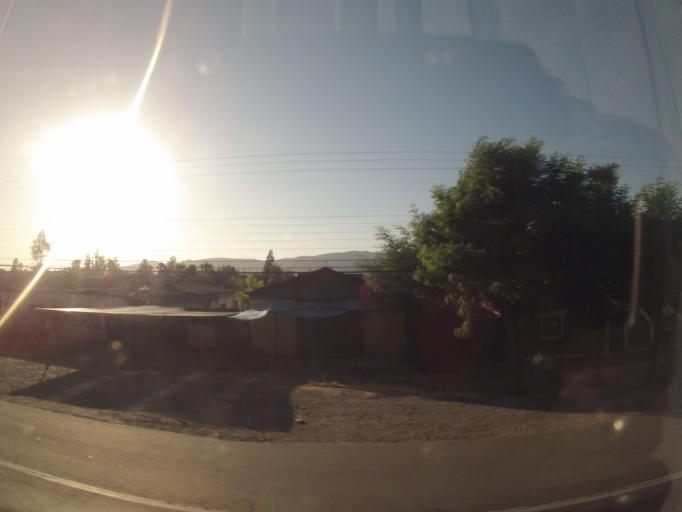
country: CL
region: O'Higgins
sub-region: Provincia de Colchagua
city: Chimbarongo
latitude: -34.7121
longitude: -71.0294
